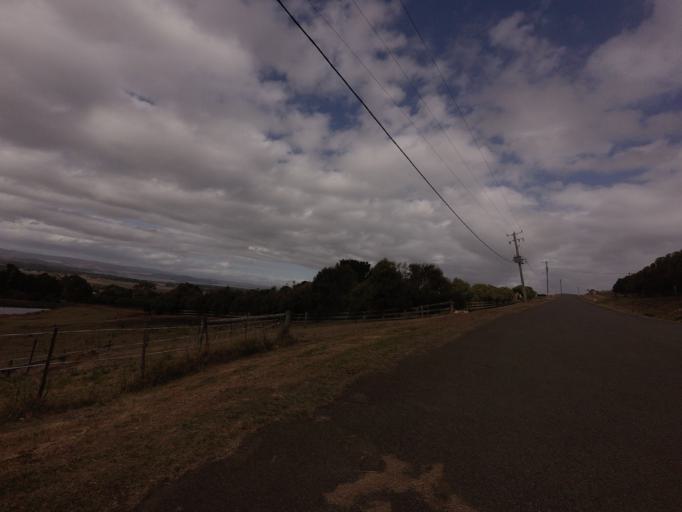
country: AU
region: Tasmania
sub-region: Clarence
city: Cambridge
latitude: -42.8576
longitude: 147.4650
